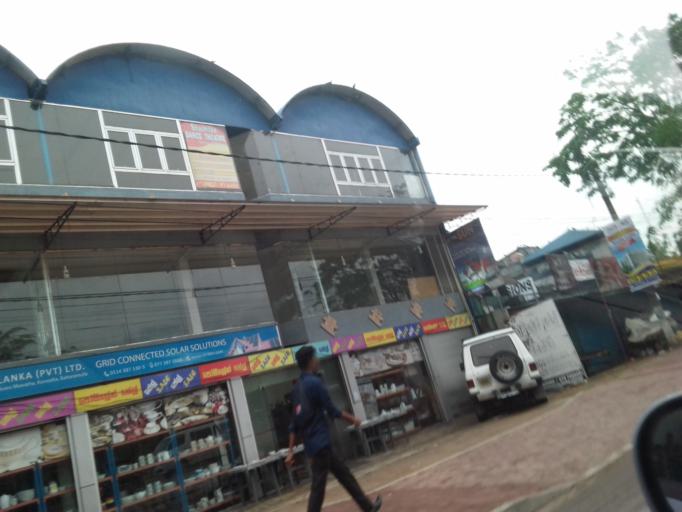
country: LK
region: Western
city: Battaramulla South
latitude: 6.9058
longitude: 79.9293
